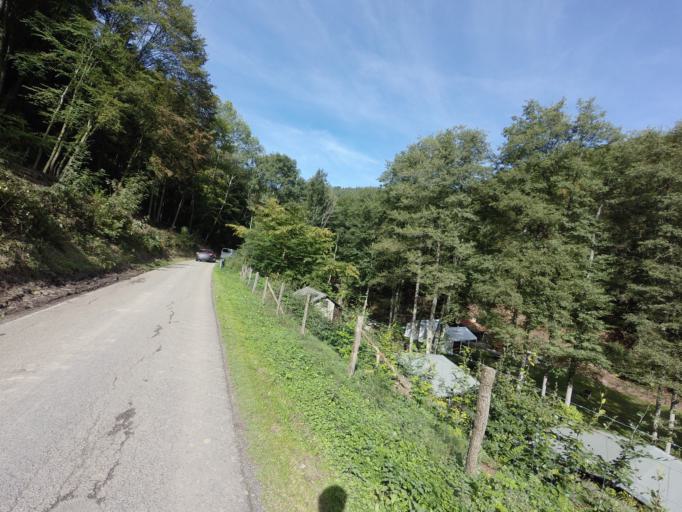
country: DE
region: North Rhine-Westphalia
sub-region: Regierungsbezirk Koln
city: Hurtgenwald
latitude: 50.6386
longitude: 6.3856
